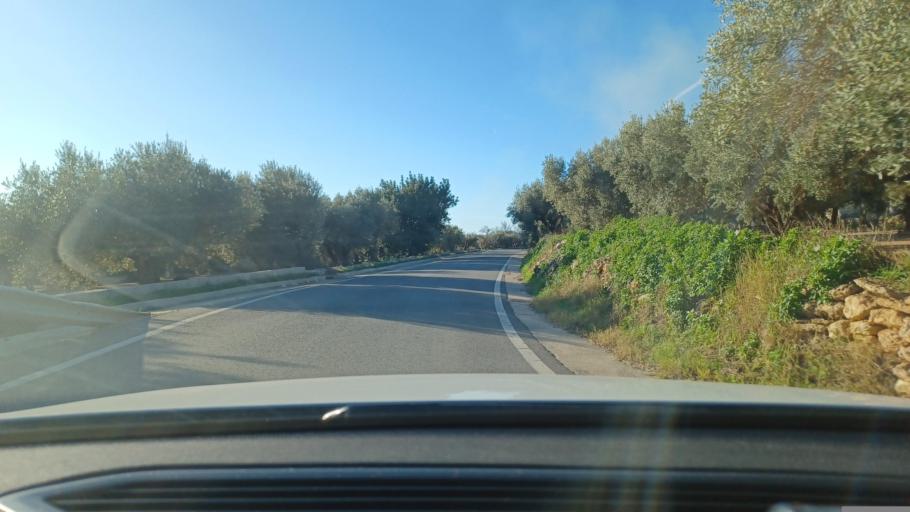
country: ES
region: Catalonia
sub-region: Provincia de Tarragona
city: Mas de Barberans
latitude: 40.7240
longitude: 0.3675
